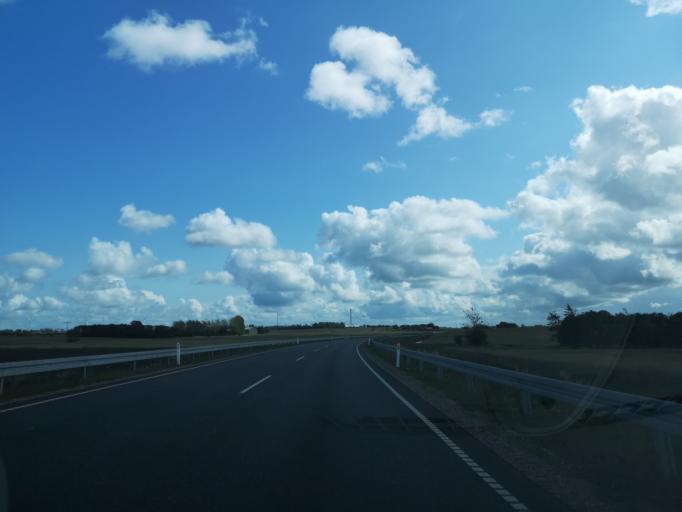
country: DK
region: Central Jutland
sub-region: Holstebro Kommune
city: Holstebro
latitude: 56.3956
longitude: 8.5711
